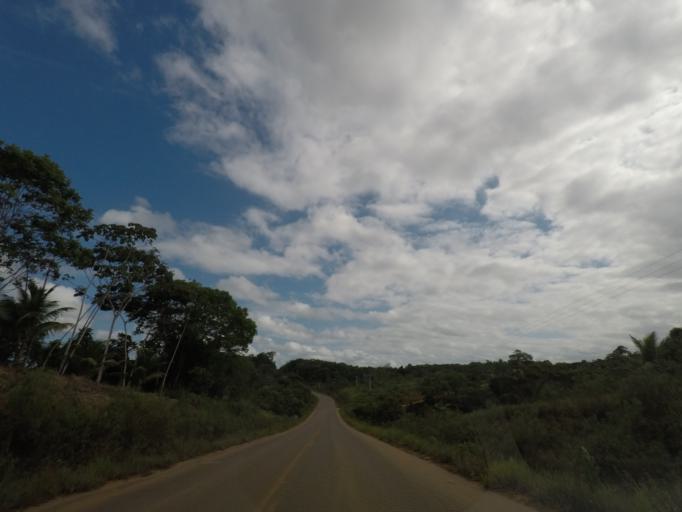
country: BR
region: Bahia
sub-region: Itacare
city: Itacare
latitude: -14.2142
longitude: -39.1009
